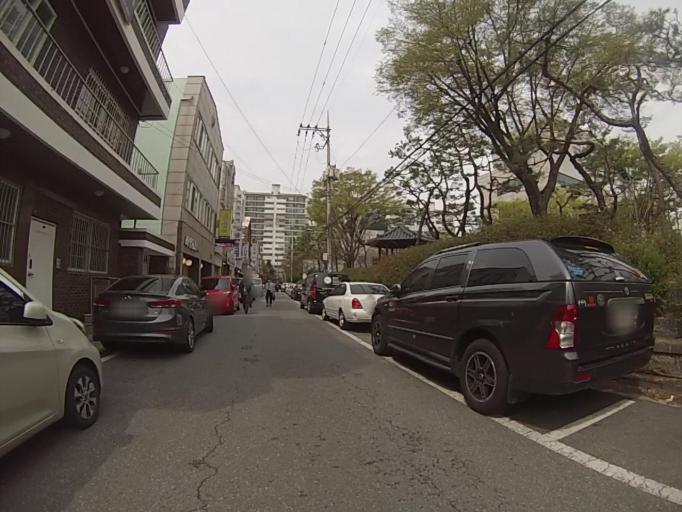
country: KR
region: Daejeon
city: Songgang-dong
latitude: 36.3626
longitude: 127.3557
